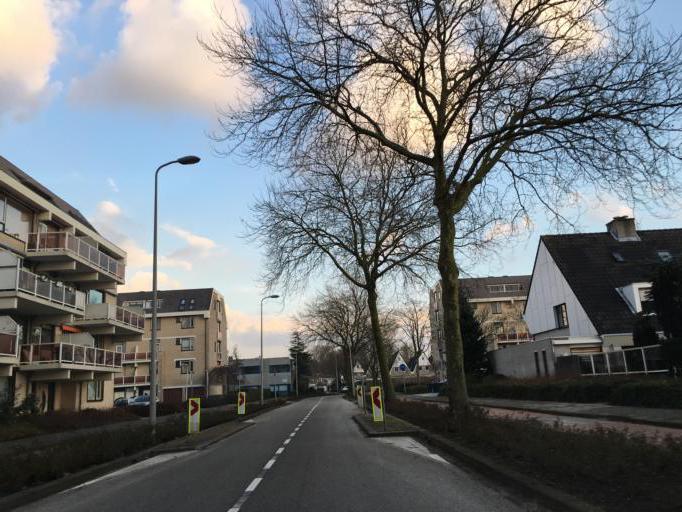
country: NL
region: South Holland
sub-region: Gemeente Capelle aan den IJssel
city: Capelle aan den IJssel
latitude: 51.9390
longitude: 4.5654
